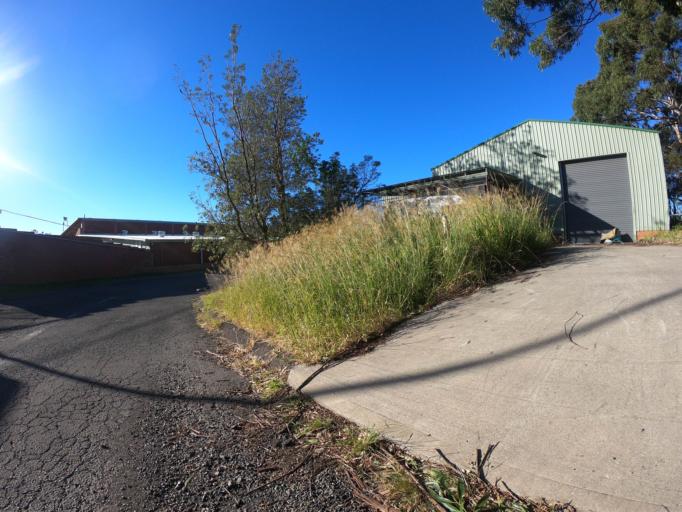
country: AU
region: New South Wales
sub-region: Wollongong
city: Bulli
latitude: -34.3301
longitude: 150.9104
